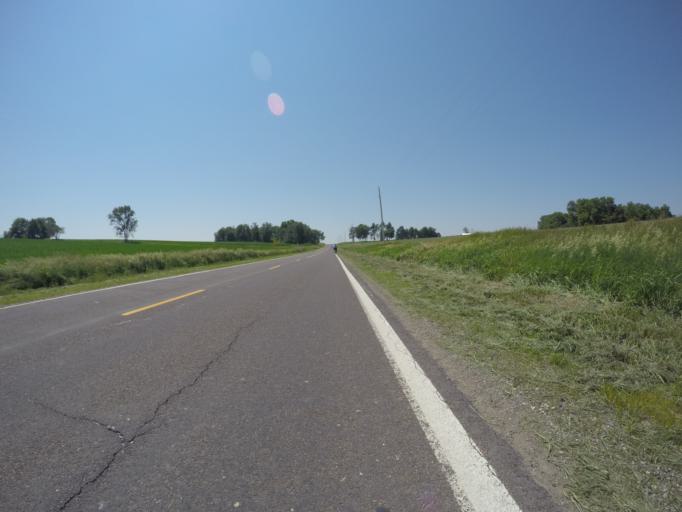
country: US
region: Kansas
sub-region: Doniphan County
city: Highland
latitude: 39.8359
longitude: -95.2653
